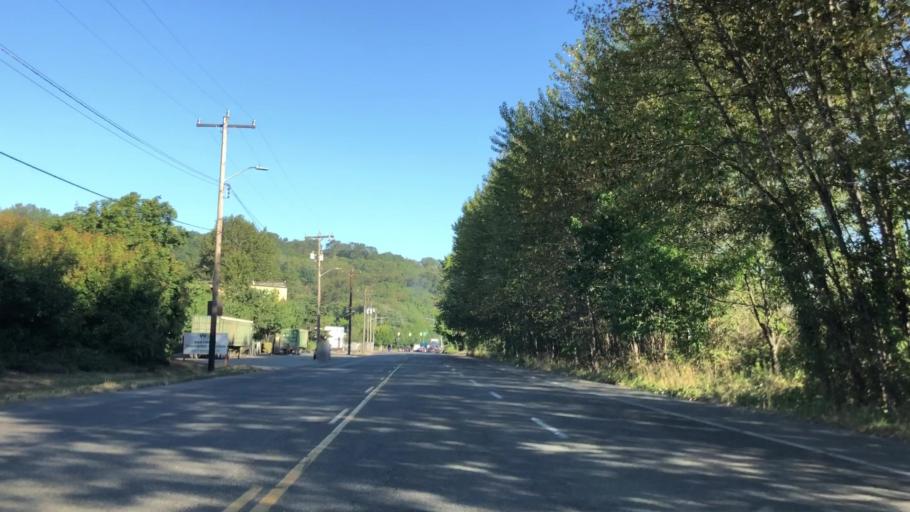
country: US
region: Washington
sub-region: King County
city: White Center
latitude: 47.5380
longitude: -122.3381
